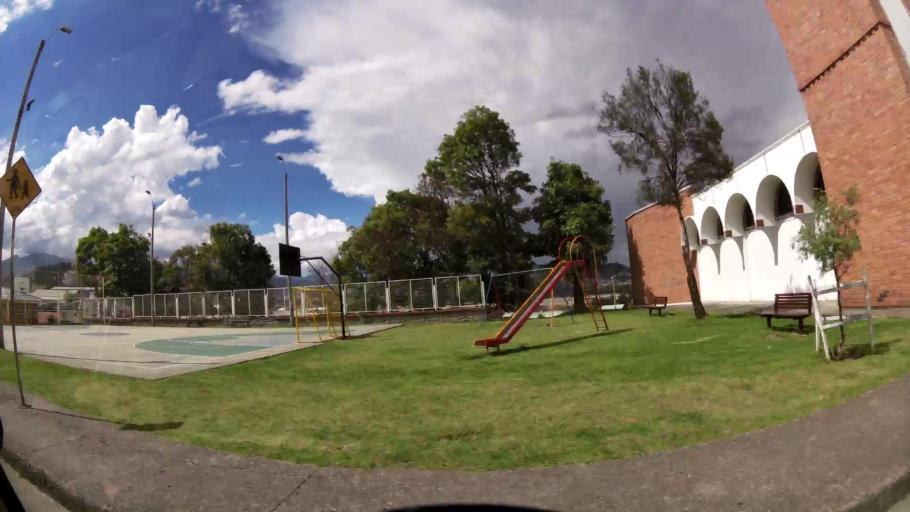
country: EC
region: Azuay
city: Cuenca
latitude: -2.8797
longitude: -78.9798
